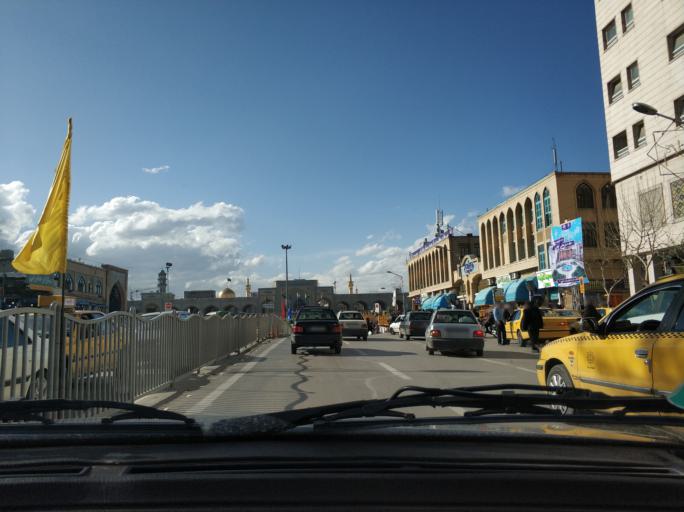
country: IR
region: Razavi Khorasan
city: Mashhad
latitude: 36.2854
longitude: 59.6195
